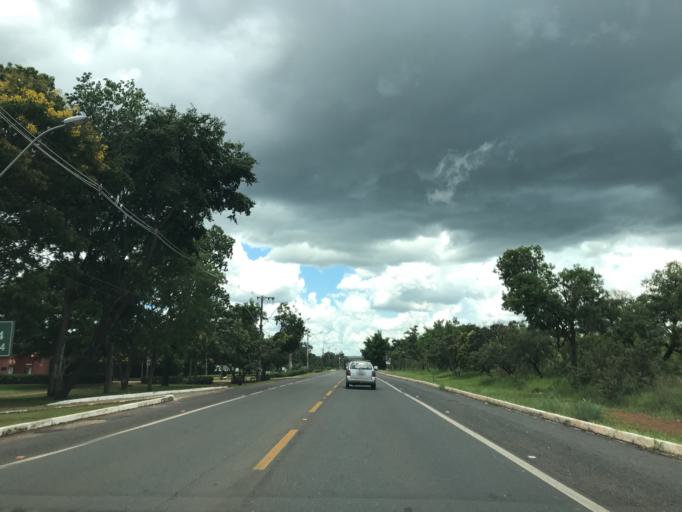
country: BR
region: Federal District
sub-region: Brasilia
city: Brasilia
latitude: -15.8892
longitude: -47.9526
